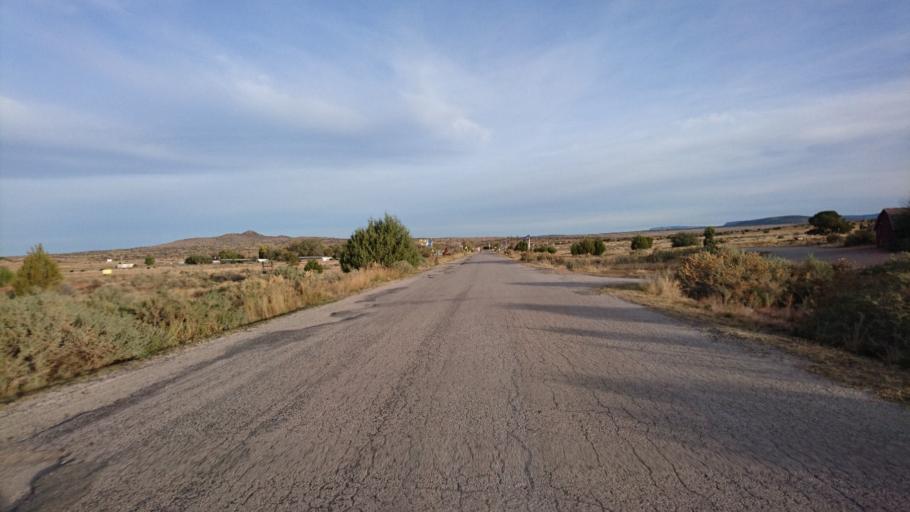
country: US
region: Arizona
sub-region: Mohave County
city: Peach Springs
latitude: 35.5257
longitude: -113.2286
